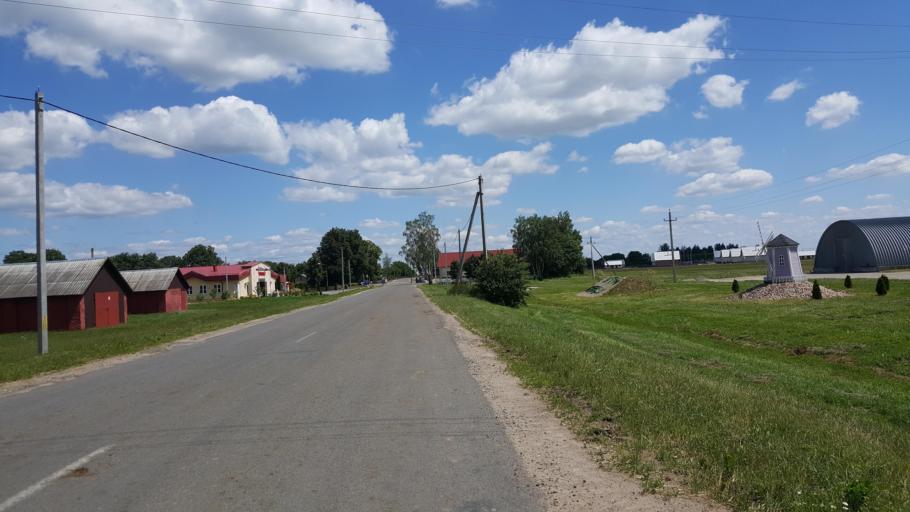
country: PL
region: Podlasie
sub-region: Powiat hajnowski
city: Czeremcha
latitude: 52.4910
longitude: 23.4325
